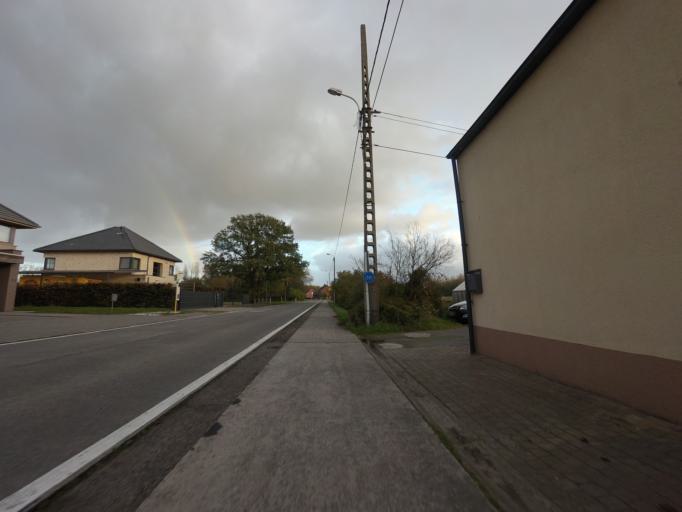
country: BE
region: Flanders
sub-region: Provincie Antwerpen
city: Putte
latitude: 51.0336
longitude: 4.5957
